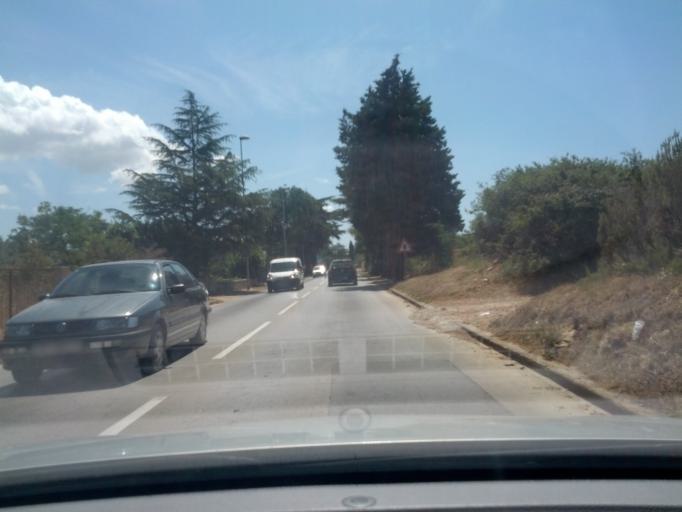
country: HR
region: Istarska
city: Fazana
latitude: 44.9114
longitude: 13.8200
